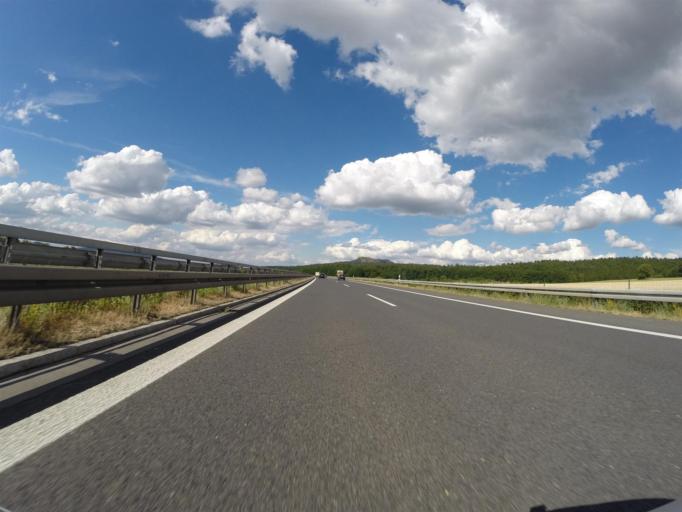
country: DE
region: Bavaria
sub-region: Upper Franconia
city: Bad Staffelstein
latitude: 50.0721
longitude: 10.9923
